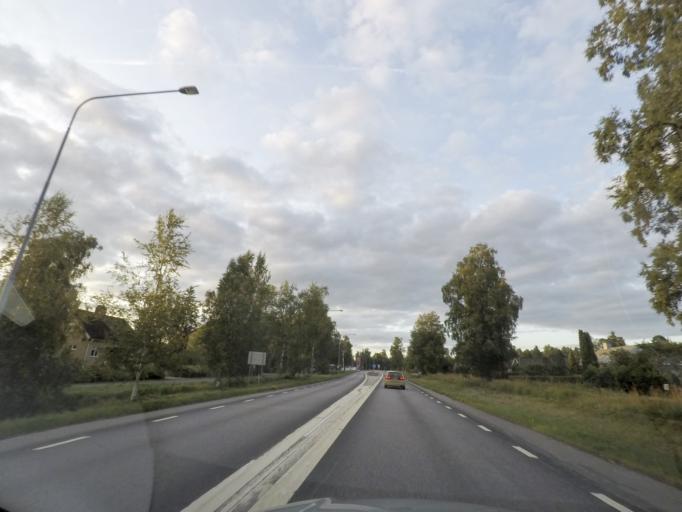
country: SE
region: OErebro
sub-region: Hallefors Kommun
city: Haellefors
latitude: 59.7837
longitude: 14.5321
